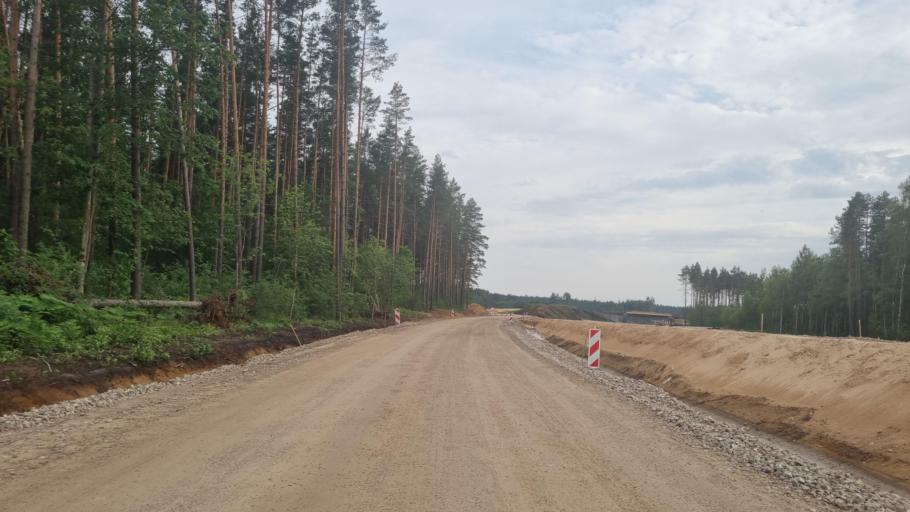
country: LV
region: Kekava
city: Balozi
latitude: 56.8699
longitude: 24.1679
